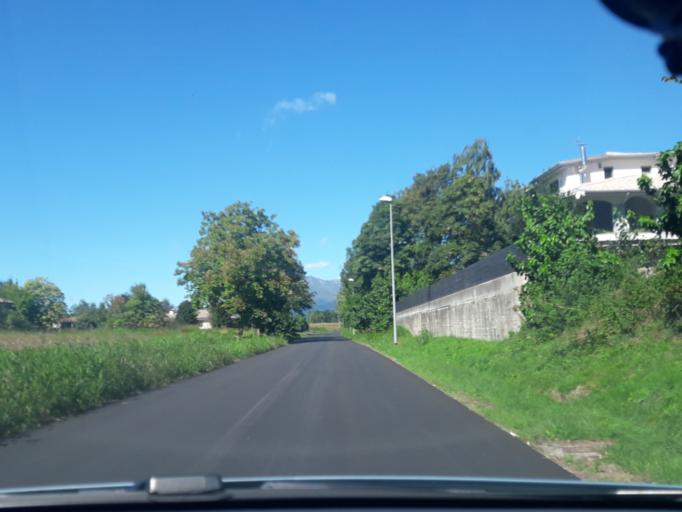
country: IT
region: Friuli Venezia Giulia
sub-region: Provincia di Udine
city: Reana del Roiale
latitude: 46.1413
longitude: 13.2155
